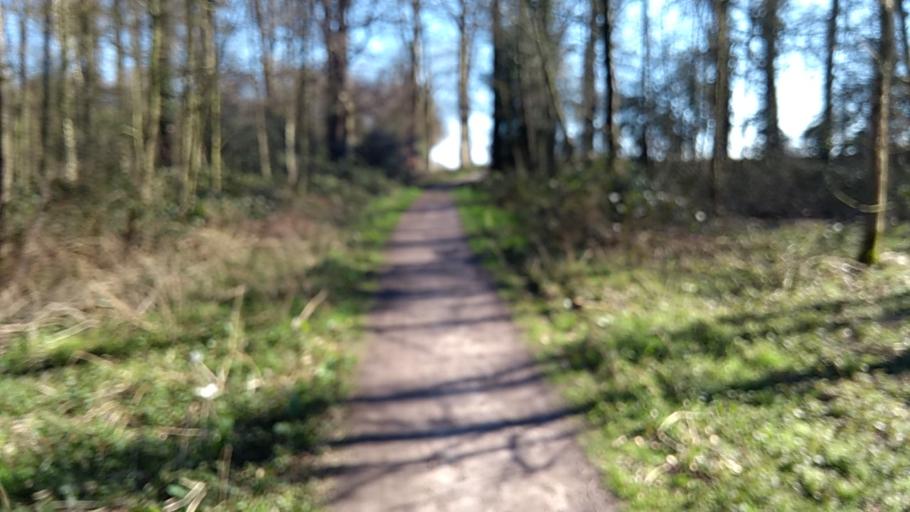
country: NL
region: Overijssel
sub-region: Gemeente Hof van Twente
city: Delden
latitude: 52.2807
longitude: 6.7022
